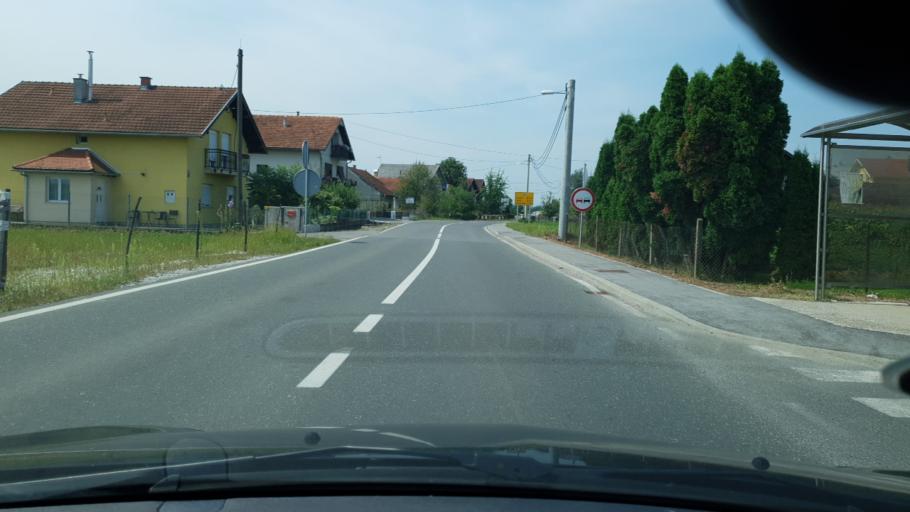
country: HR
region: Krapinsko-Zagorska
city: Bedekovcina
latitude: 46.0373
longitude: 15.9804
